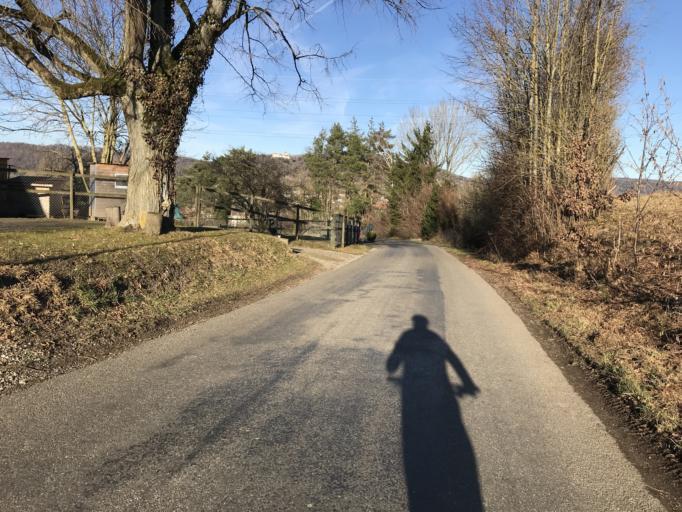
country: CH
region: Thurgau
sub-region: Frauenfeld District
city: Wagenhausen
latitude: 47.6483
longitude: 8.8485
